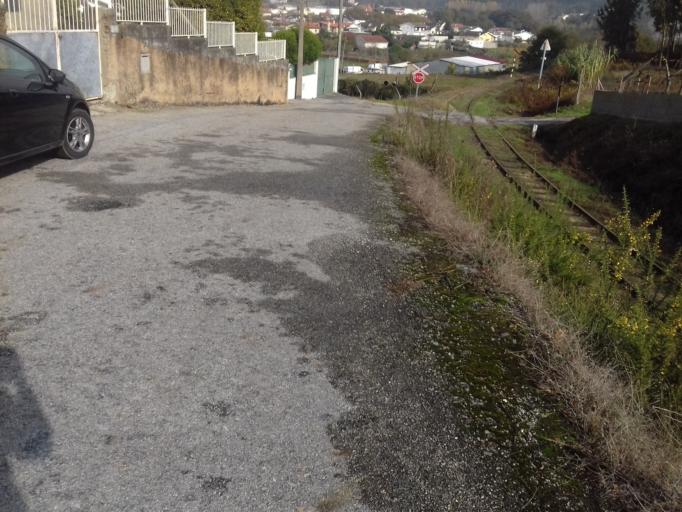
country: PT
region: Aveiro
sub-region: Albergaria-A-Velha
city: Branca
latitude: 40.7772
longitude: -8.4870
